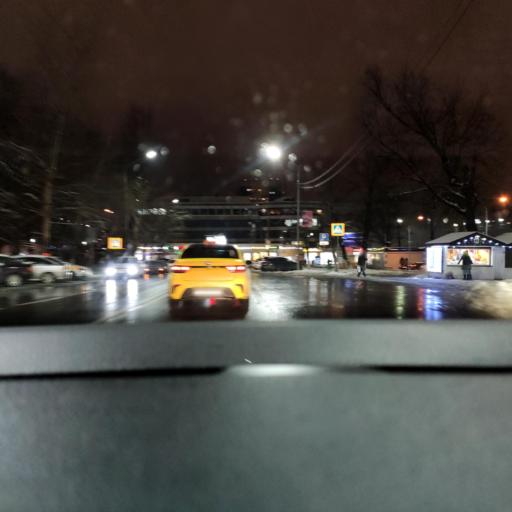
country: RU
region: Moskovskaya
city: Reutov
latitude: 55.7537
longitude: 37.8587
